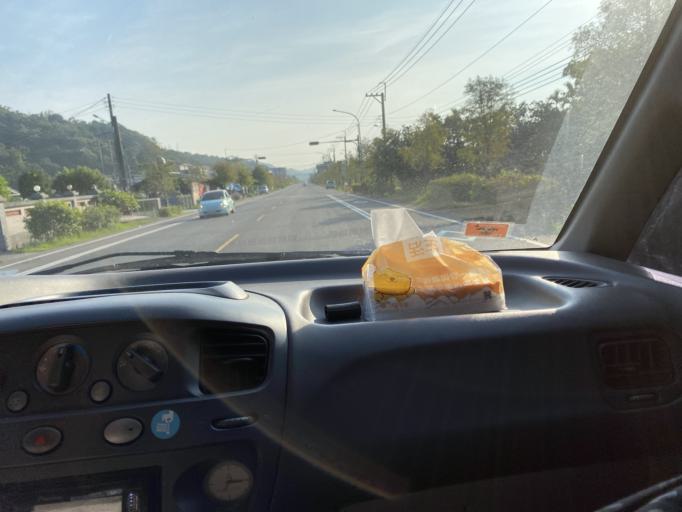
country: TW
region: Taiwan
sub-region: Keelung
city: Keelung
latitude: 25.0258
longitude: 121.8234
